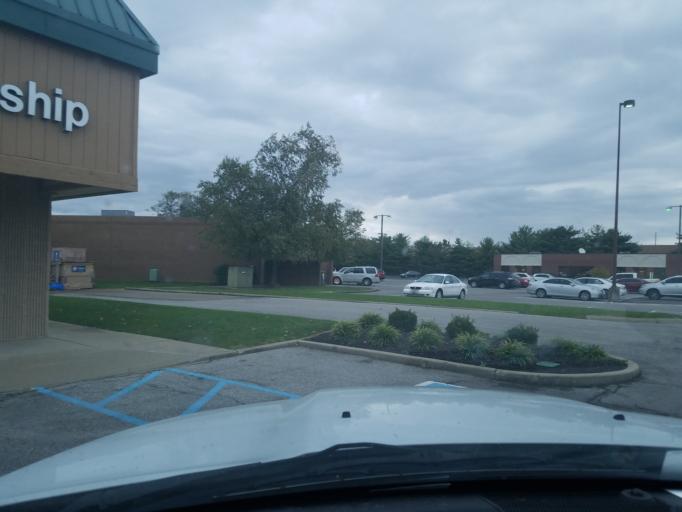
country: US
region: Indiana
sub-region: Vanderburgh County
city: Melody Hill
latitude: 37.9815
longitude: -87.4910
